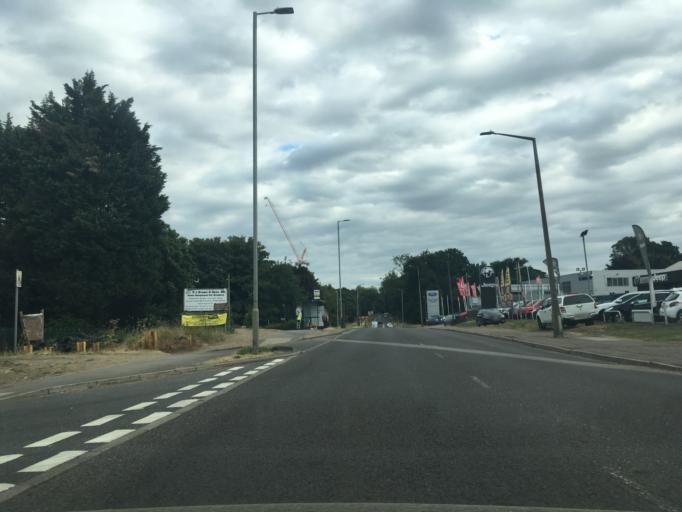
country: GB
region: England
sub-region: Hertfordshire
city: Hemel Hempstead
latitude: 51.7697
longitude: -0.4489
